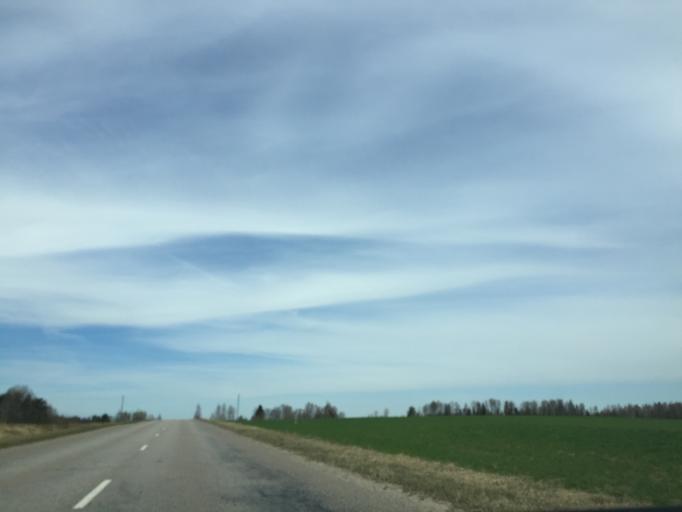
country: LV
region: Valkas Rajons
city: Valka
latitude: 57.7833
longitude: 25.9079
